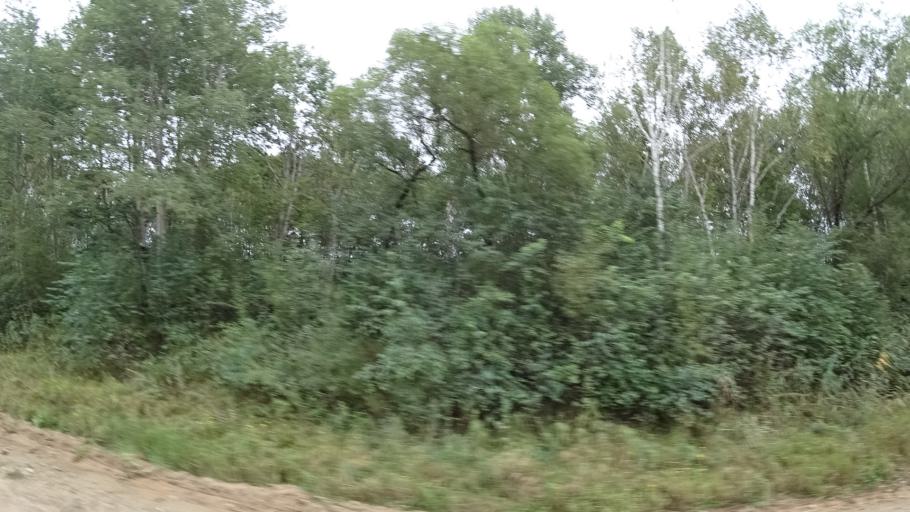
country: RU
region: Primorskiy
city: Rettikhovka
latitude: 44.1472
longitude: 132.6763
